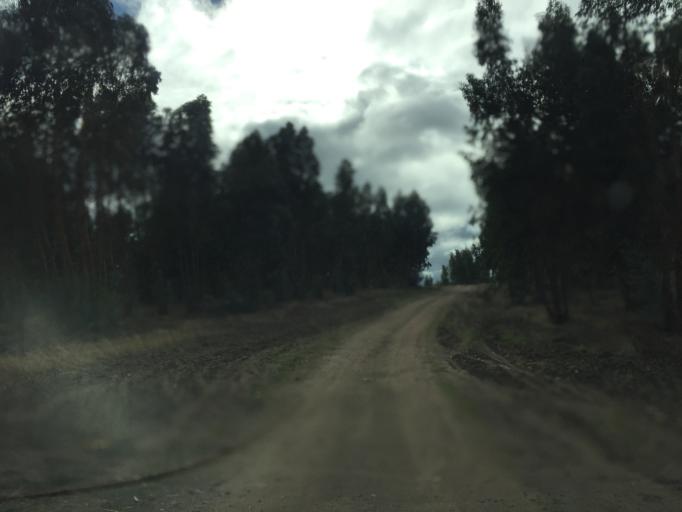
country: PT
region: Portalegre
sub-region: Alter do Chao
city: Alter do Chao
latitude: 39.2450
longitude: -7.7034
